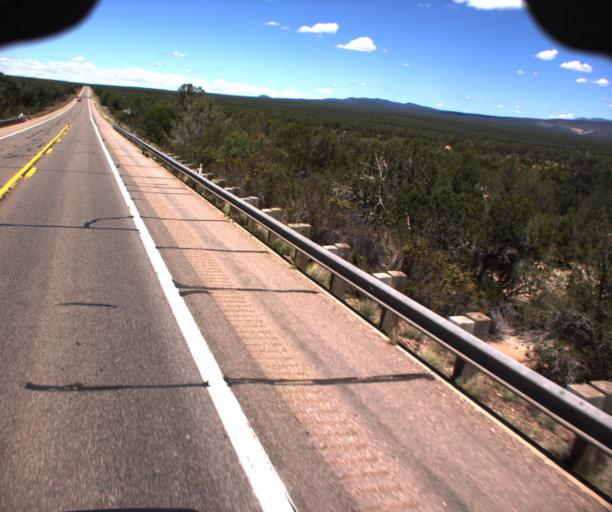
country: US
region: Arizona
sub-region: Yavapai County
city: Paulden
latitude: 35.0142
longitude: -112.3914
